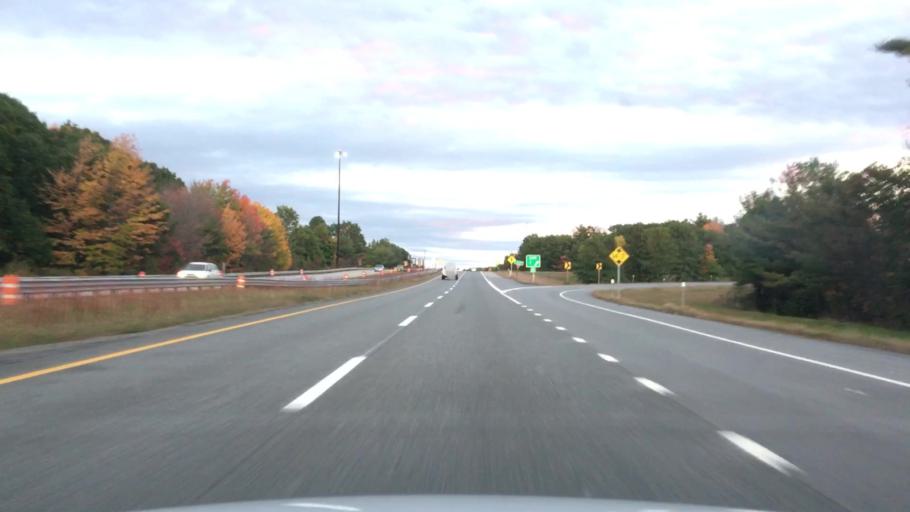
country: US
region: Maine
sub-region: Cumberland County
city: South Portland Gardens
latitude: 43.6263
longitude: -70.3328
